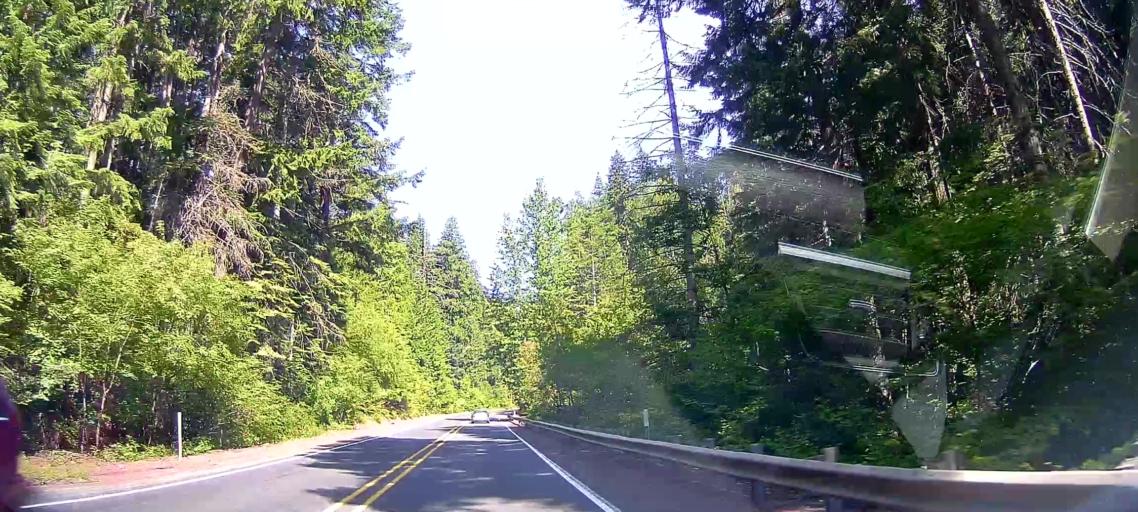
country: US
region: Oregon
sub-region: Jefferson County
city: Warm Springs
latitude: 45.1035
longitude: -121.5537
